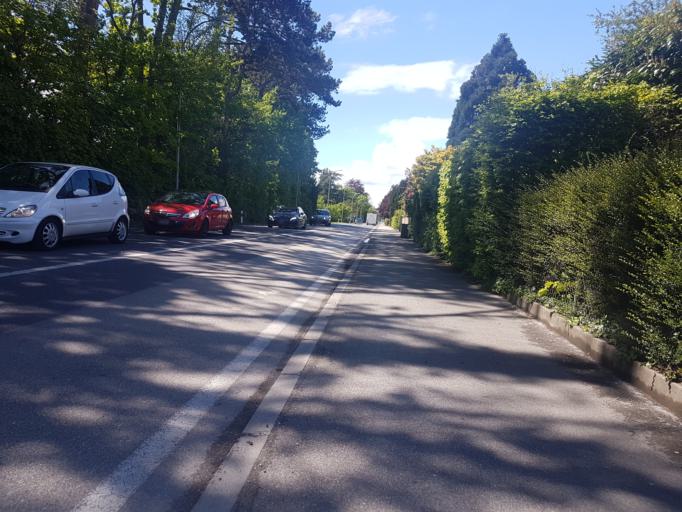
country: CH
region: Vaud
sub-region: Nyon District
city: Prangins
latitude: 46.3943
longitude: 6.2559
